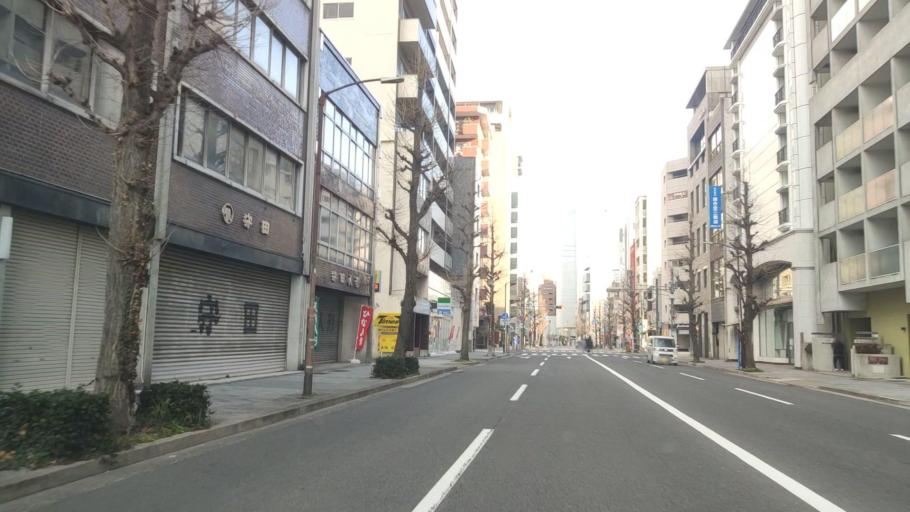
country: JP
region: Aichi
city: Nagoya-shi
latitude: 35.1632
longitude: 136.9023
